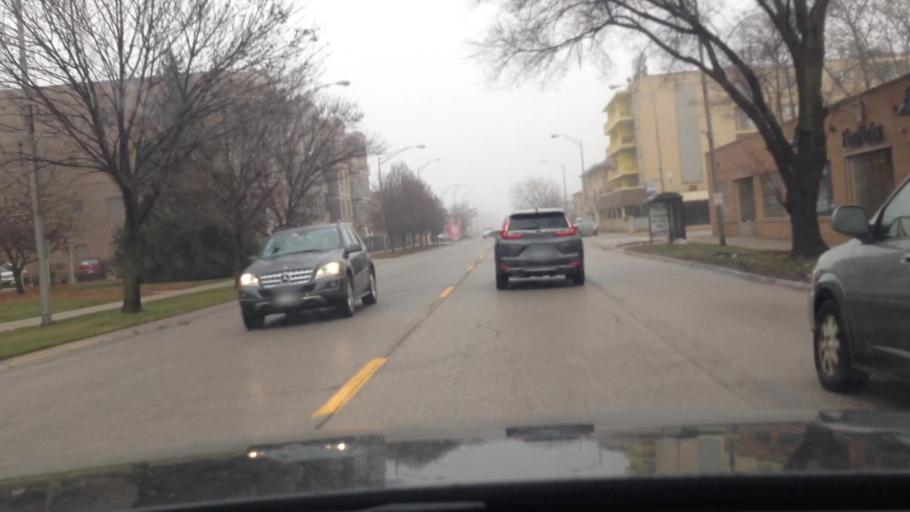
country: US
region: Illinois
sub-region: Cook County
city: River Grove
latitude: 41.9271
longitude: -87.8259
